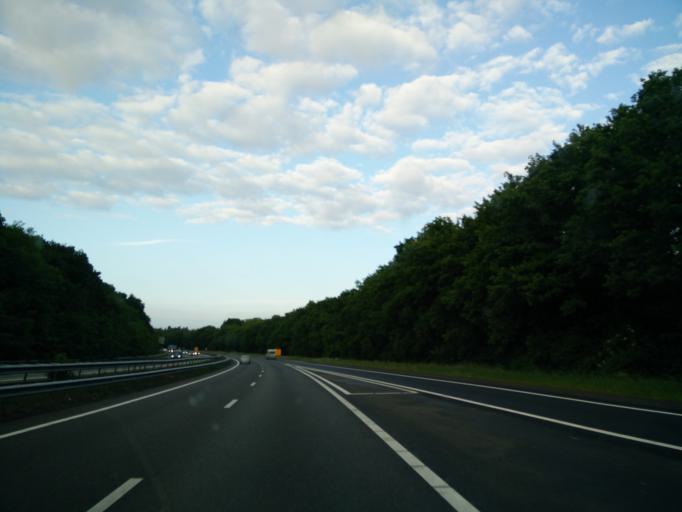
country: NL
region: Gelderland
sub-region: Gemeente Harderwijk
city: Harderwijk
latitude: 52.3296
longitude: 5.6233
